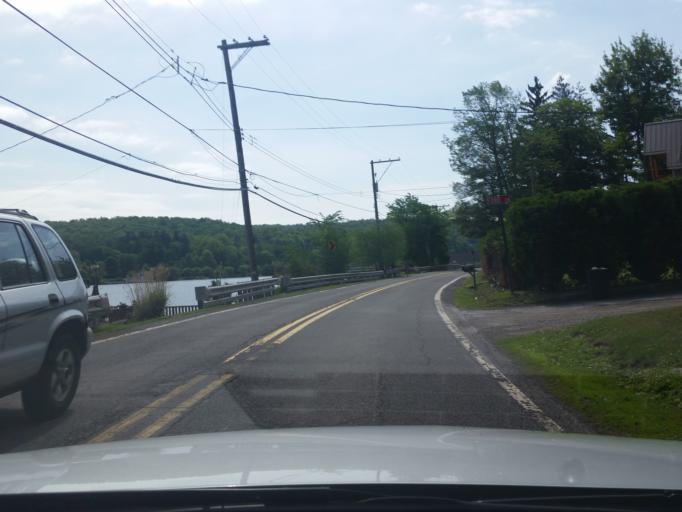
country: US
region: Pennsylvania
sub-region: Luzerne County
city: Harveys Lake
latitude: 41.3658
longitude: -76.0457
